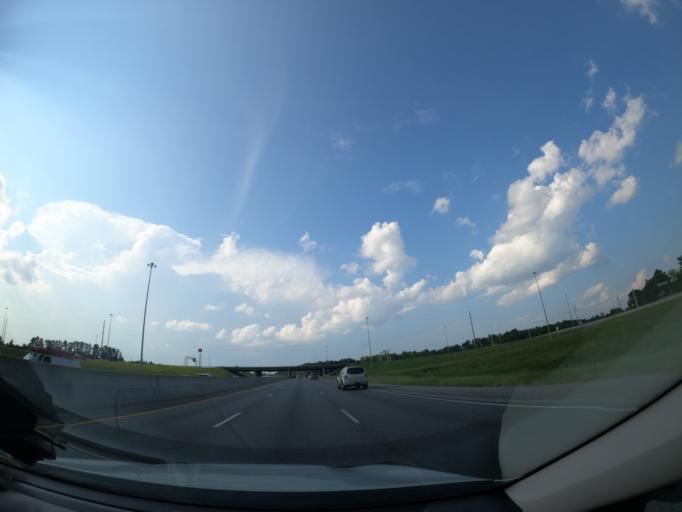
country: US
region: Georgia
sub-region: Columbia County
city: Martinez
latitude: 33.4487
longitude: -82.0732
